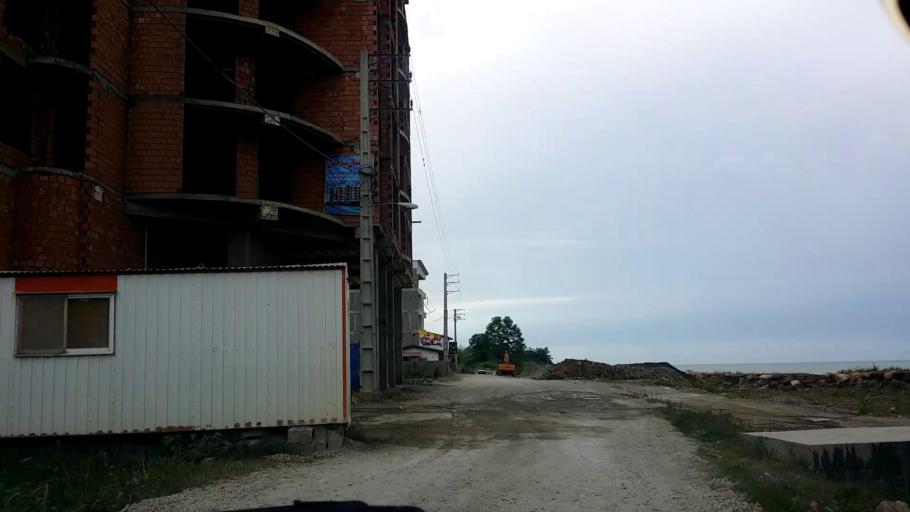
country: IR
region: Mazandaran
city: Chalus
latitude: 36.6836
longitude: 51.4318
